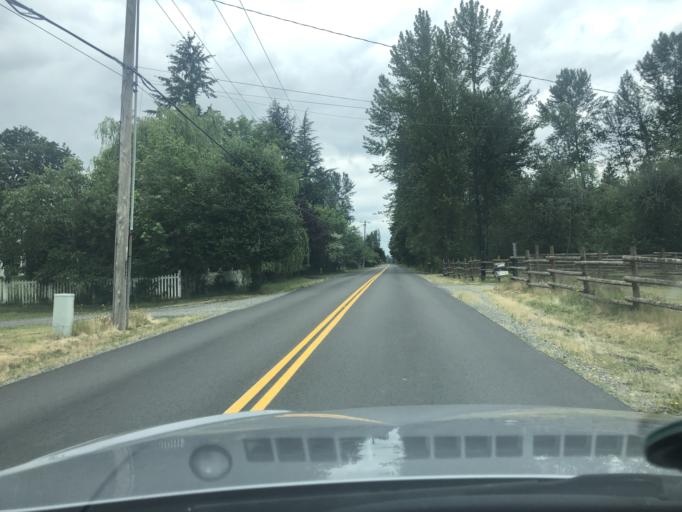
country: US
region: Washington
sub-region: King County
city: Lake Morton-Berrydale
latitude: 47.3298
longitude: -122.0912
